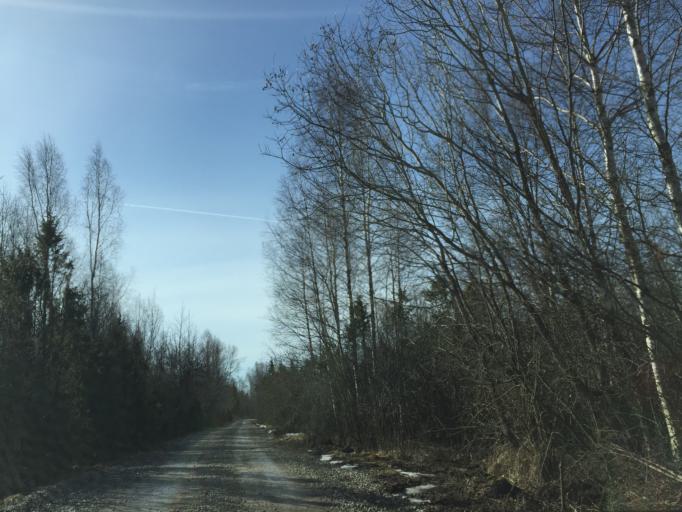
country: EE
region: Laeaene
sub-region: Haapsalu linn
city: Haapsalu
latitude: 58.6636
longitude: 23.5198
